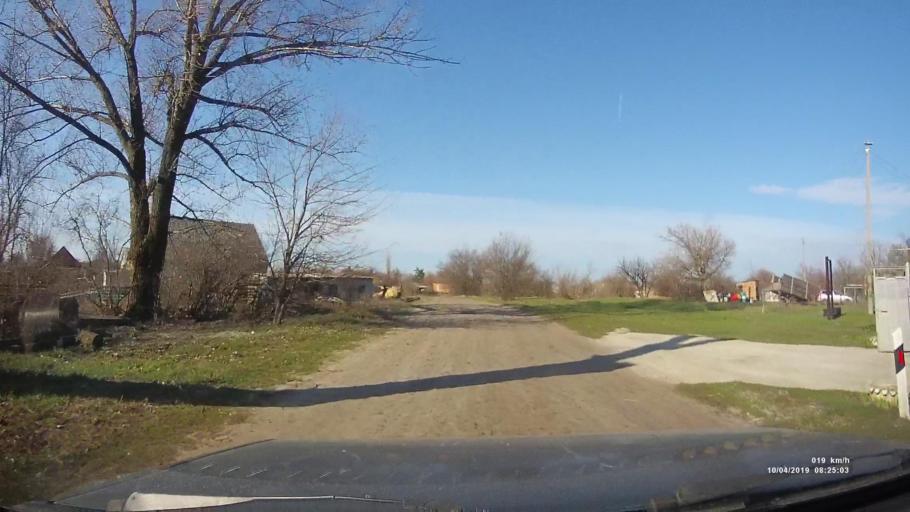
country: RU
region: Rostov
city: Kamensk-Shakhtinskiy
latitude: 48.3589
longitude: 40.2343
